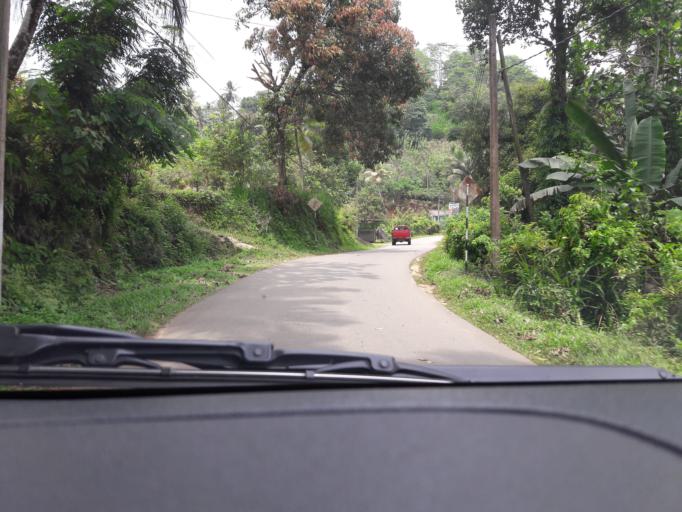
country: LK
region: Southern
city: Galle
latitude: 6.1759
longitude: 80.2883
